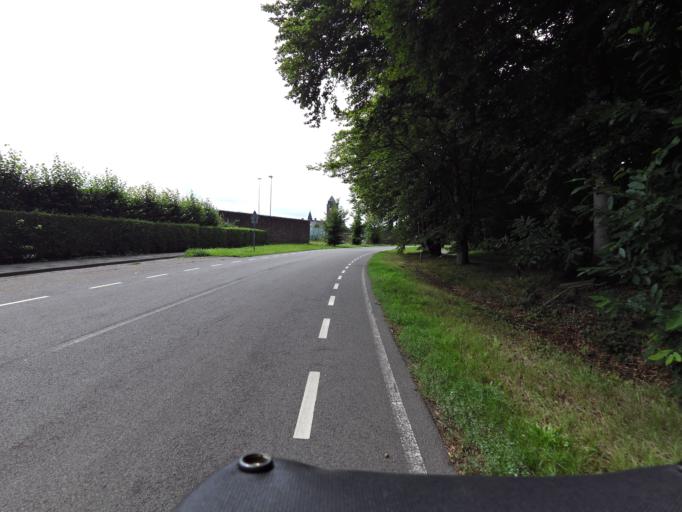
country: NL
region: North Brabant
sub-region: Gemeente Breda
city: Breda
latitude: 51.5749
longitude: 4.6999
